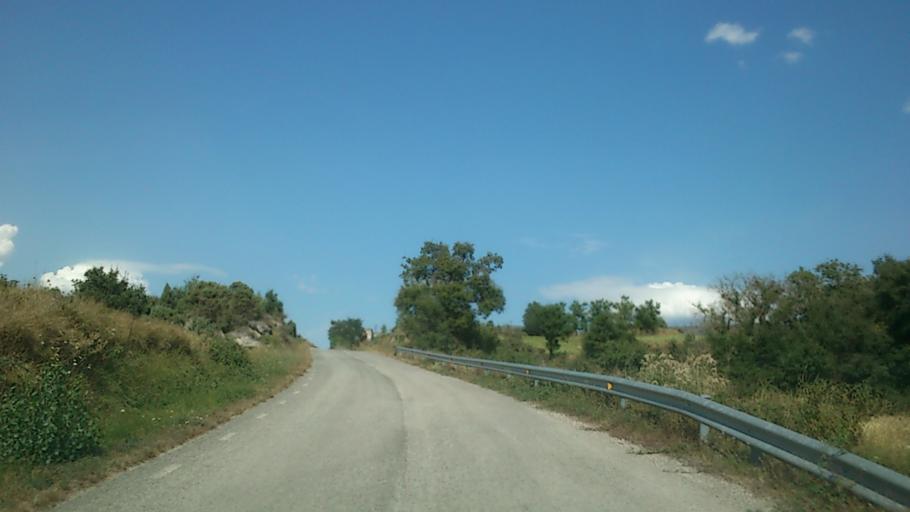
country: ES
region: Castille and Leon
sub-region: Provincia de Burgos
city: Frias
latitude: 42.7992
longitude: -3.2625
